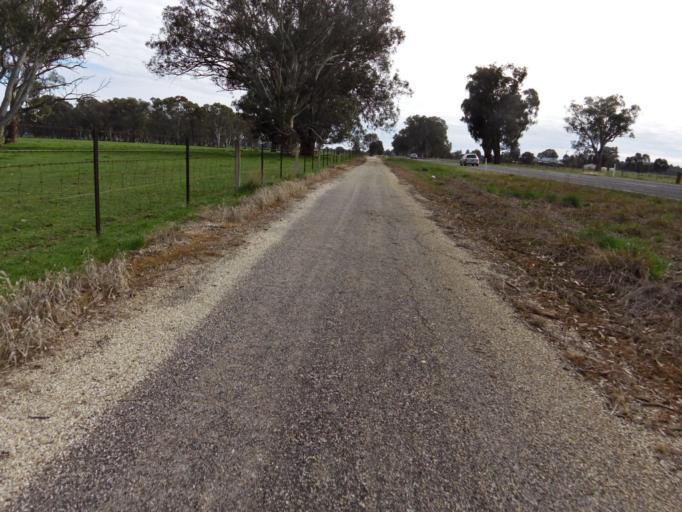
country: AU
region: Victoria
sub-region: Wangaratta
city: Wangaratta
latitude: -36.4222
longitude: 146.3577
